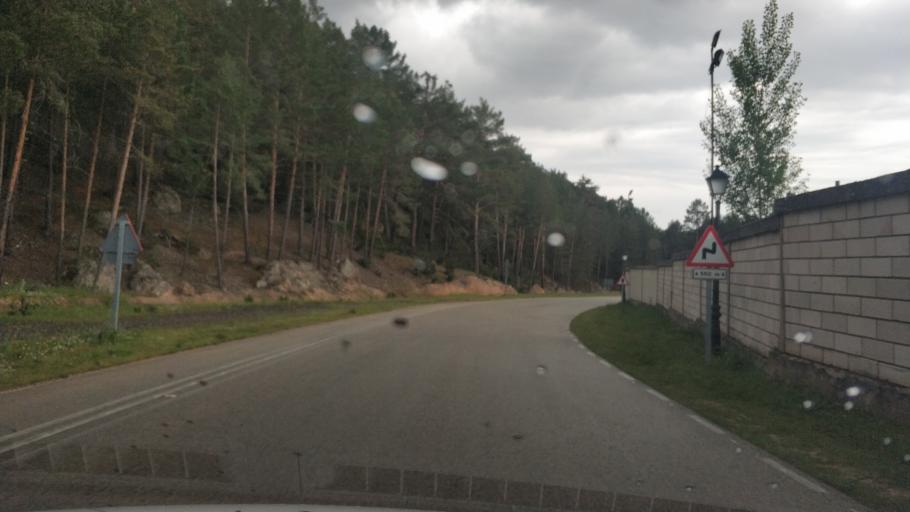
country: ES
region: Castille and Leon
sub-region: Provincia de Soria
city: San Leonardo de Yague
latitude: 41.8387
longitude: -3.0651
